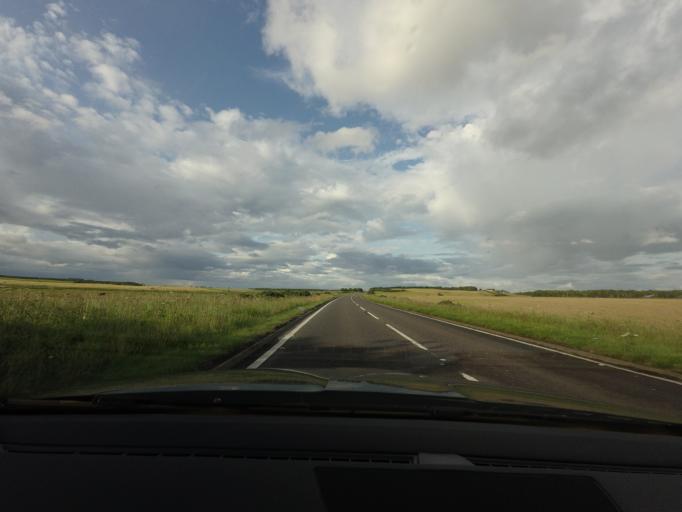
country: GB
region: Scotland
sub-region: Highland
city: Nairn
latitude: 57.5585
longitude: -3.9670
